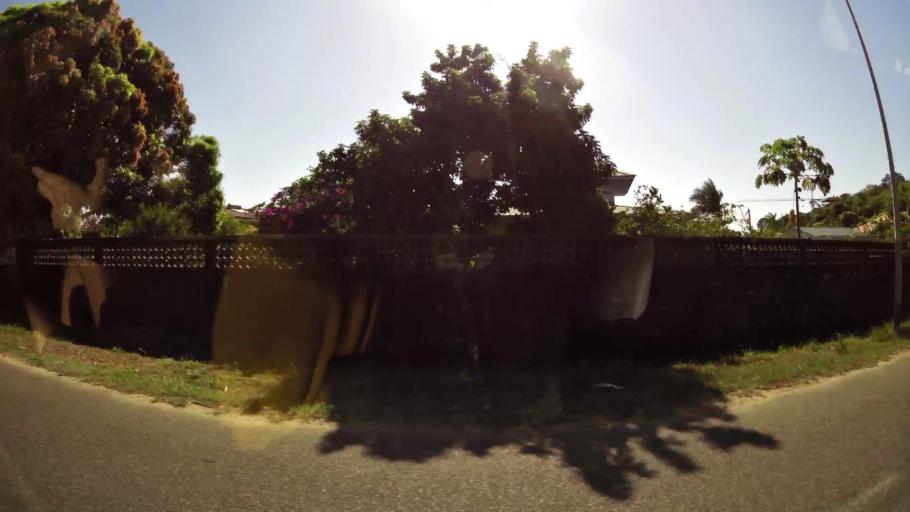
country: GF
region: Guyane
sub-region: Guyane
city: Remire-Montjoly
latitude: 4.9009
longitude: -52.2737
